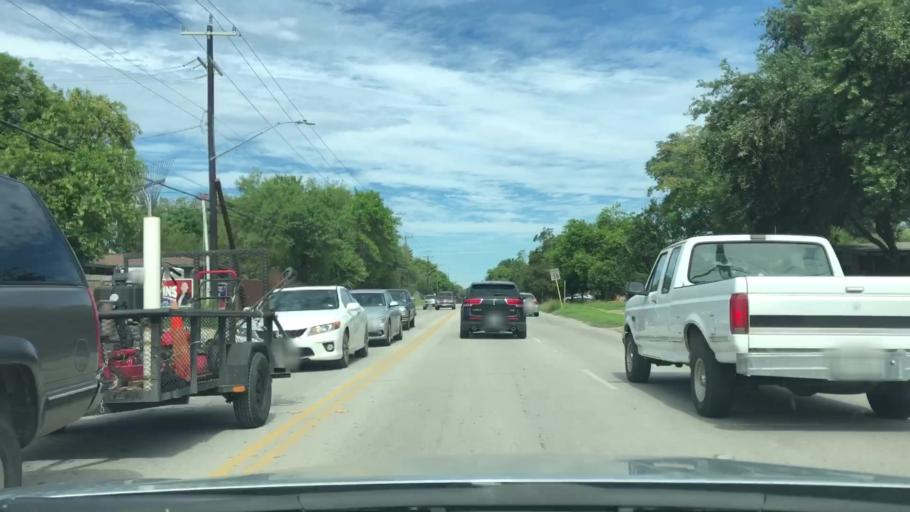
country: US
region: Texas
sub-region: Bexar County
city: Olmos Park
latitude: 29.5046
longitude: -98.4917
